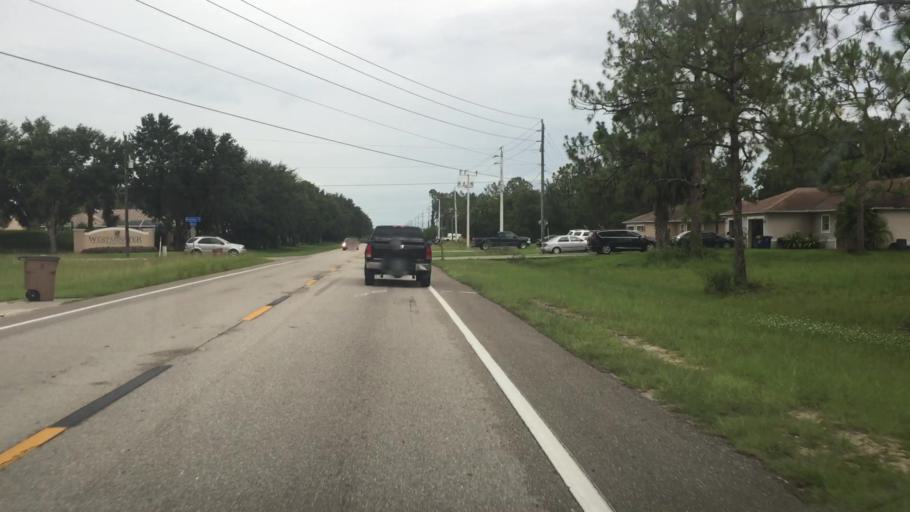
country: US
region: Florida
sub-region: Lee County
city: Gateway
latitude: 26.6039
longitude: -81.7386
